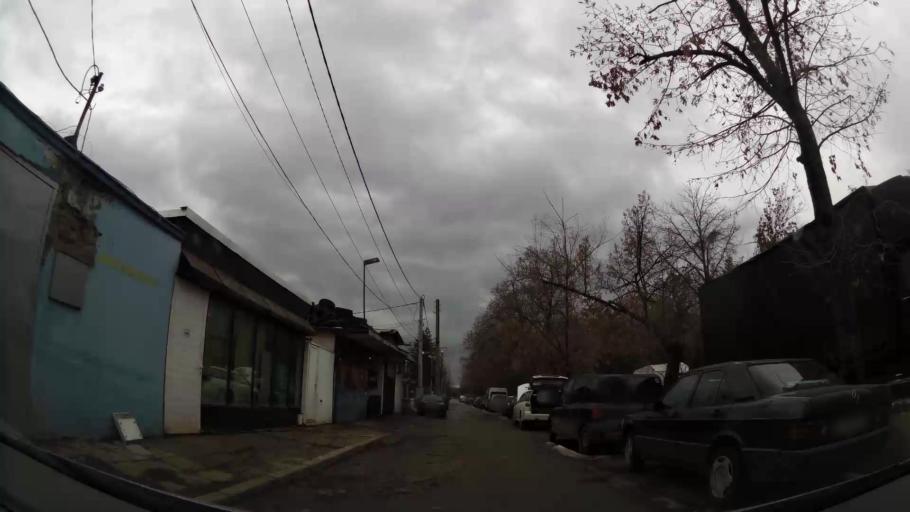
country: BG
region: Sofia-Capital
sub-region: Stolichna Obshtina
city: Sofia
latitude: 42.7215
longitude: 23.3010
